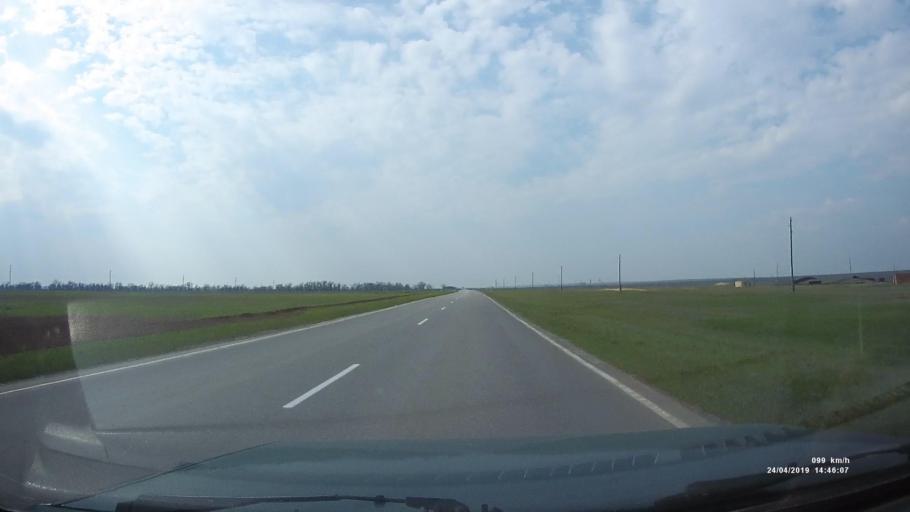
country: RU
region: Rostov
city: Remontnoye
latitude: 46.4789
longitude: 43.7957
